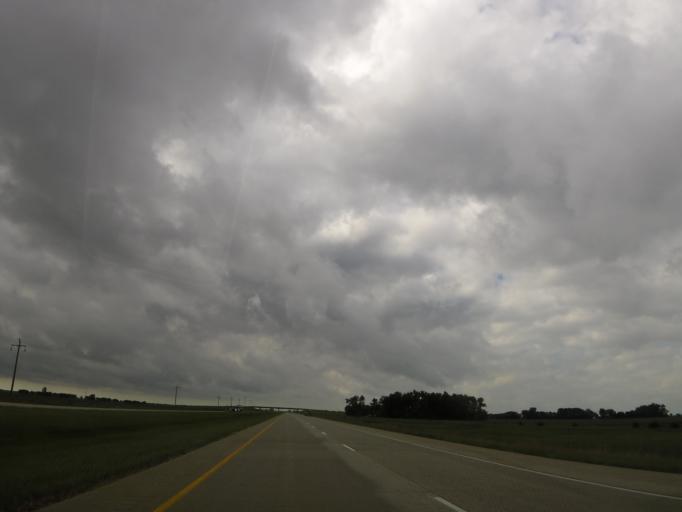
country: US
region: North Dakota
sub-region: Walsh County
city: Grafton
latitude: 48.3902
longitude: -97.1905
